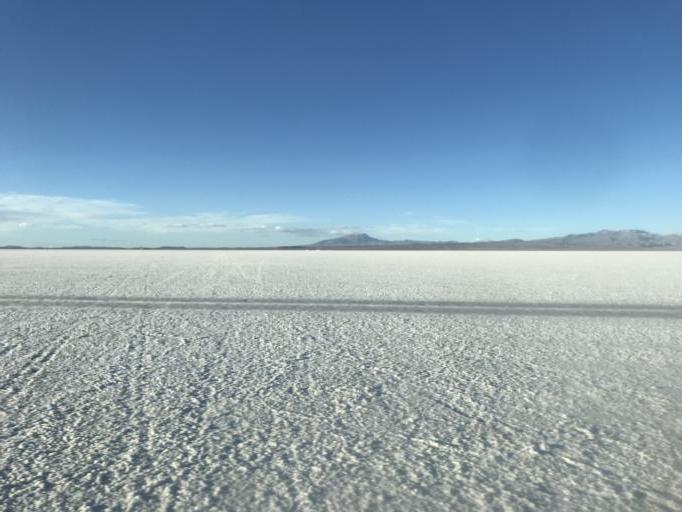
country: BO
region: Potosi
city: Colchani
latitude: -20.3643
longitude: -67.0110
